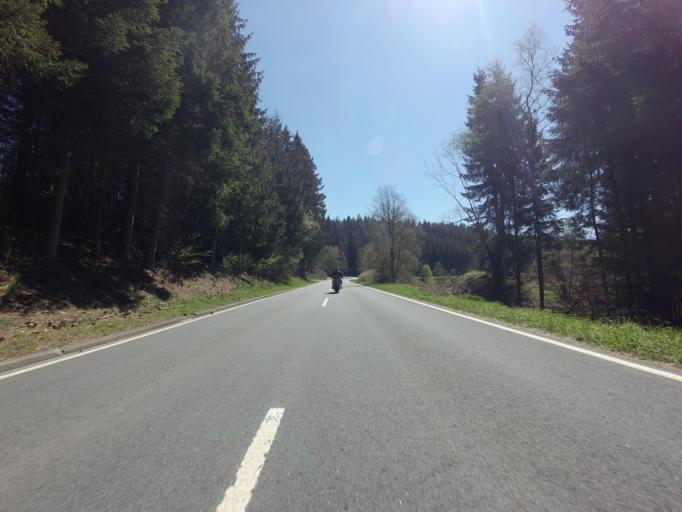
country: DE
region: North Rhine-Westphalia
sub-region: Regierungsbezirk Arnsberg
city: Erndtebruck
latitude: 51.0612
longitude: 8.2283
